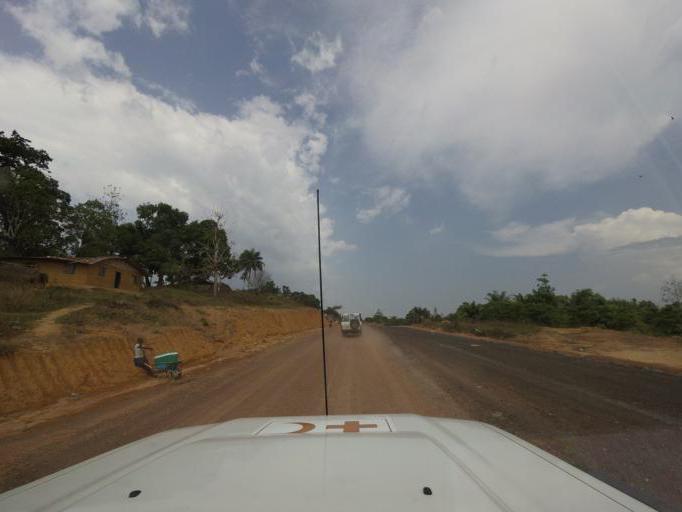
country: LR
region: Margibi
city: Kakata
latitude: 6.7498
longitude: -10.0973
